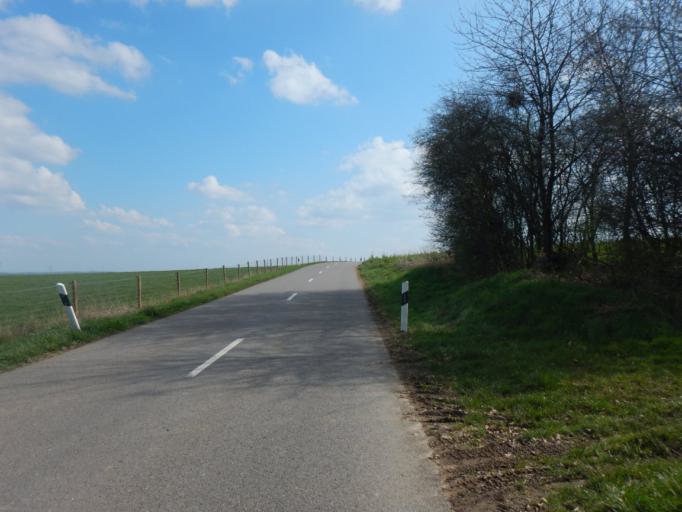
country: LU
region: Diekirch
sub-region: Canton de Diekirch
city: Medernach
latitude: 49.8090
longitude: 6.2539
